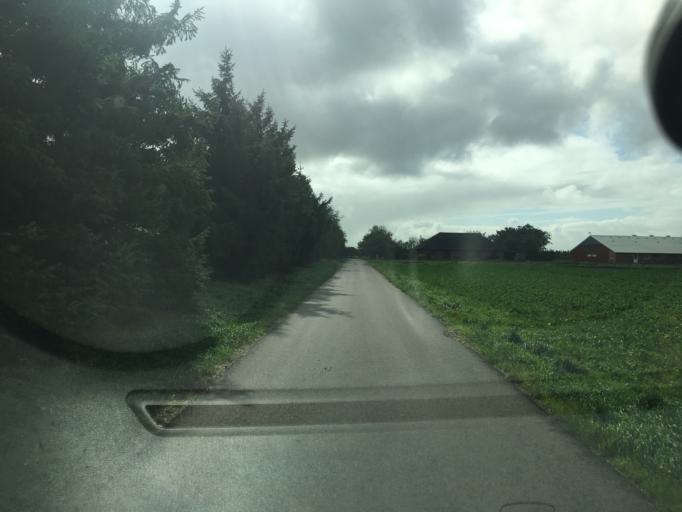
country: DK
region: South Denmark
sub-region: Tonder Kommune
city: Sherrebek
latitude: 55.0896
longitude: 8.8131
